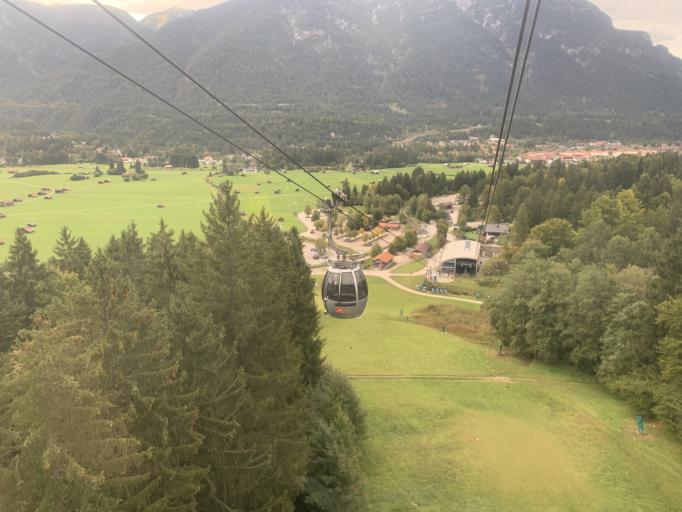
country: DE
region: Bavaria
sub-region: Upper Bavaria
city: Garmisch-Partenkirchen
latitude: 47.4688
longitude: 11.0643
